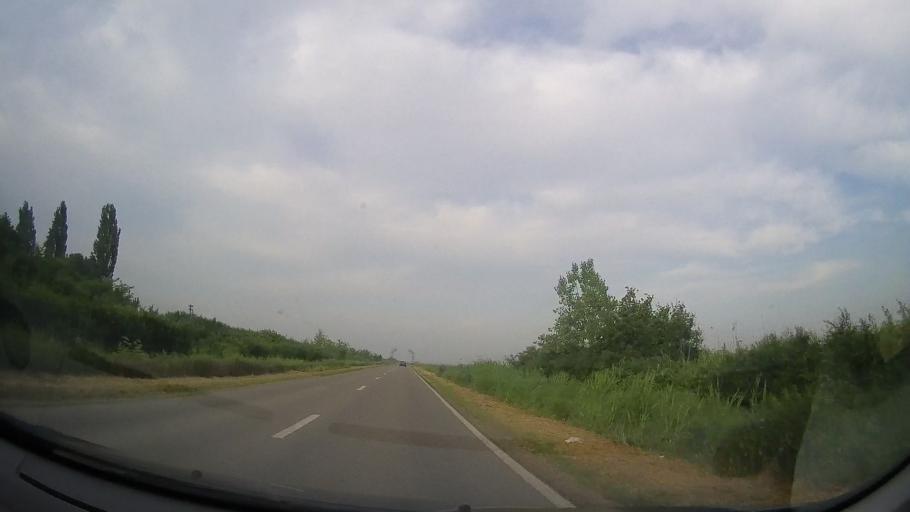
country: RO
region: Timis
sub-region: Comuna Parta
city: Parta
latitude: 45.6318
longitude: 21.1011
